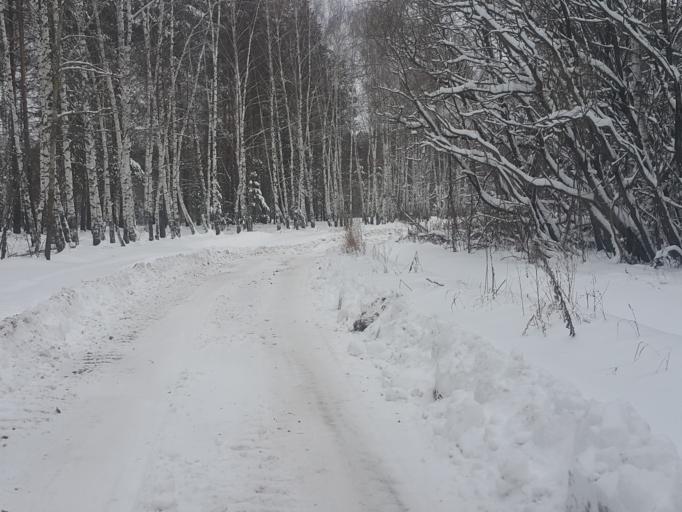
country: RU
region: Tambov
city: Platonovka
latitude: 52.8919
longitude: 41.8469
